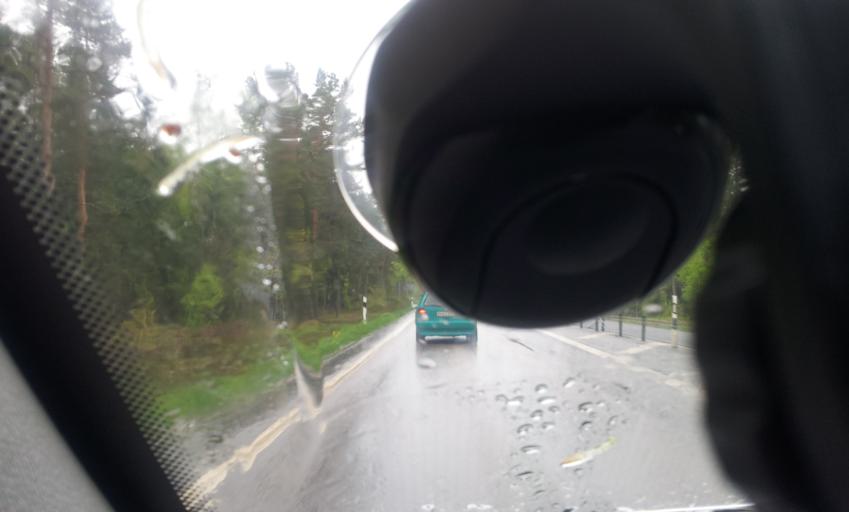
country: SE
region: Kalmar
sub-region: Oskarshamns Kommun
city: Oskarshamn
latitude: 57.3499
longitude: 16.4909
